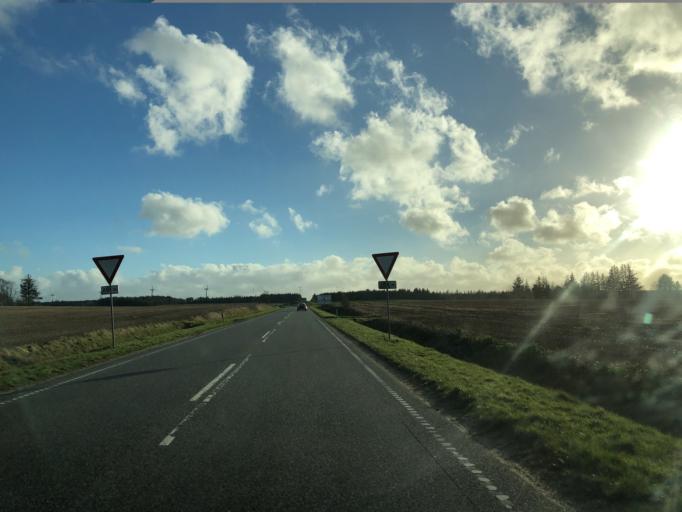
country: DK
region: Central Jutland
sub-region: Herning Kommune
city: Vildbjerg
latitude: 56.1854
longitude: 8.7047
